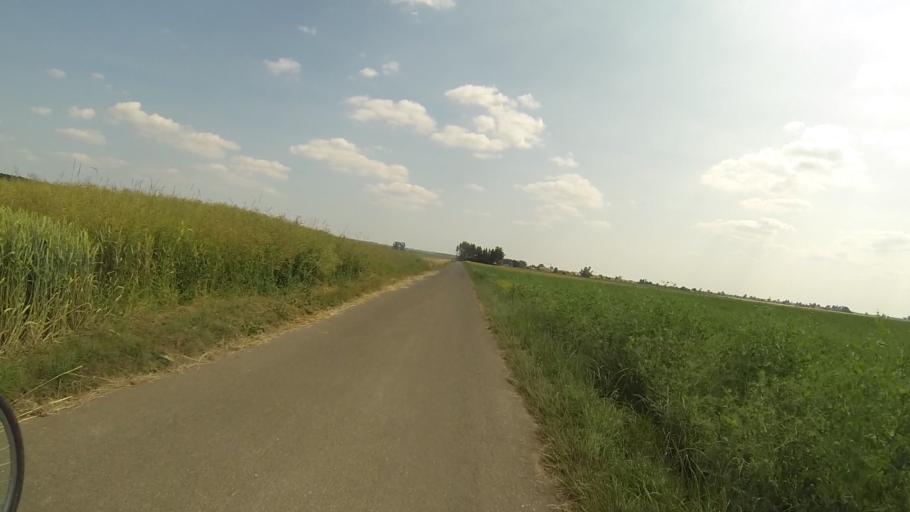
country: DE
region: Baden-Wuerttemberg
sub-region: Regierungsbezirk Stuttgart
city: Niederstotzingen
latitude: 48.5222
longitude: 10.2561
